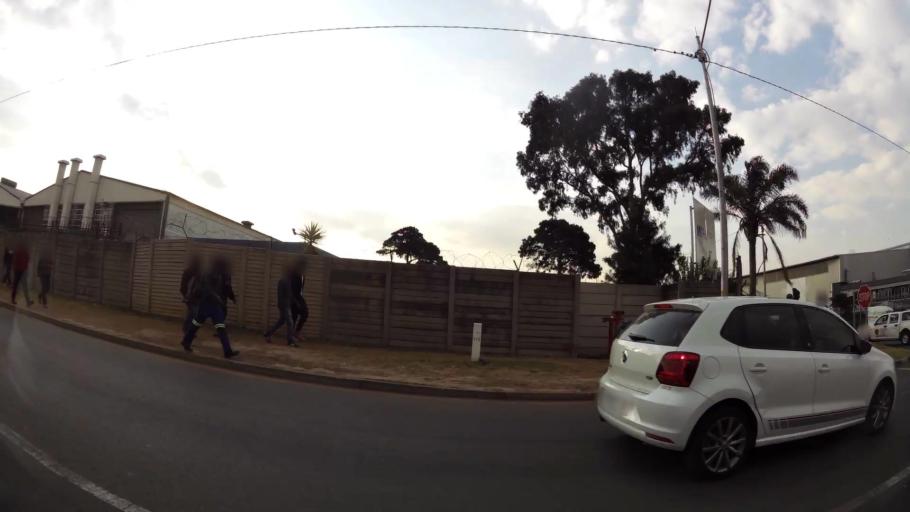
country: ZA
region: Gauteng
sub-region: Ekurhuleni Metropolitan Municipality
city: Germiston
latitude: -26.1612
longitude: 28.1900
